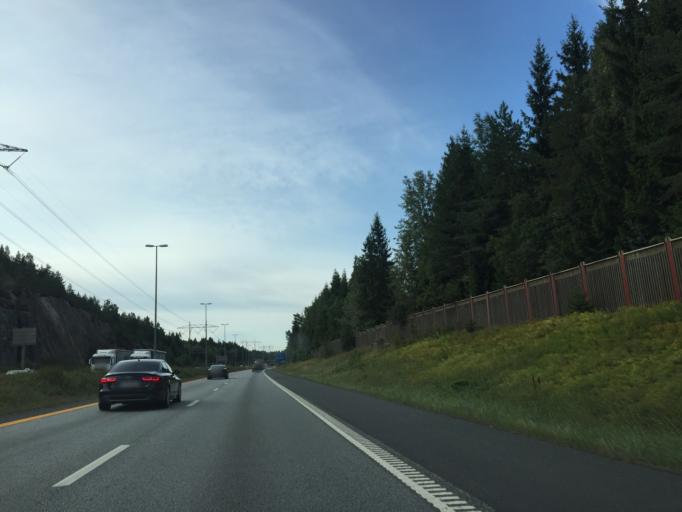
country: NO
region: Akershus
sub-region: Oppegard
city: Kolbotn
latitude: 59.8047
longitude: 10.8423
